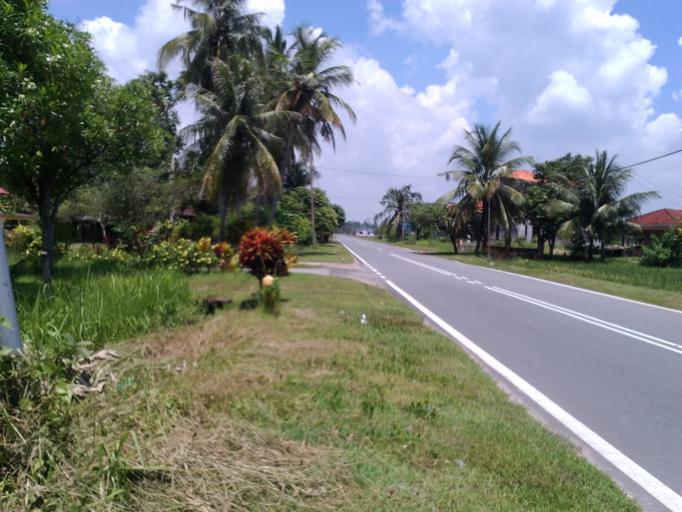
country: MY
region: Kedah
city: Jitra
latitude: 6.2049
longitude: 100.4050
